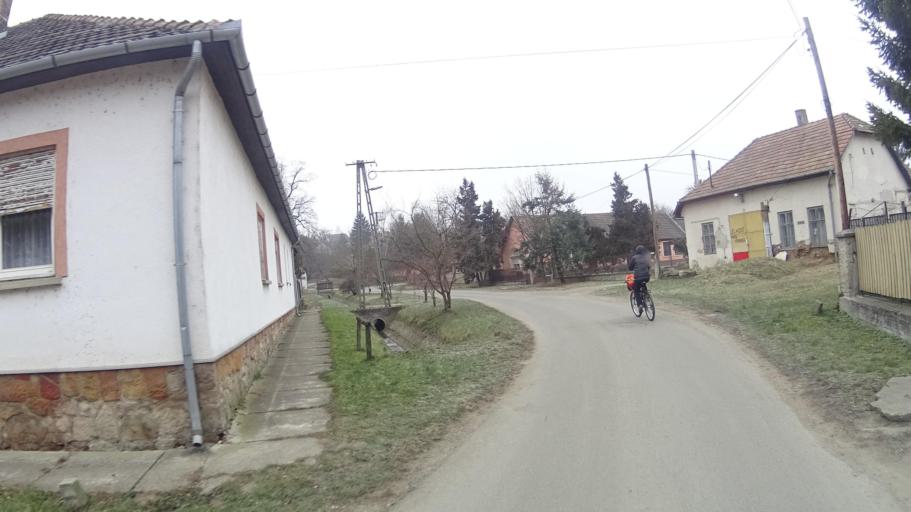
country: HU
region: Pest
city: Kosd
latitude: 47.8053
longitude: 19.1795
